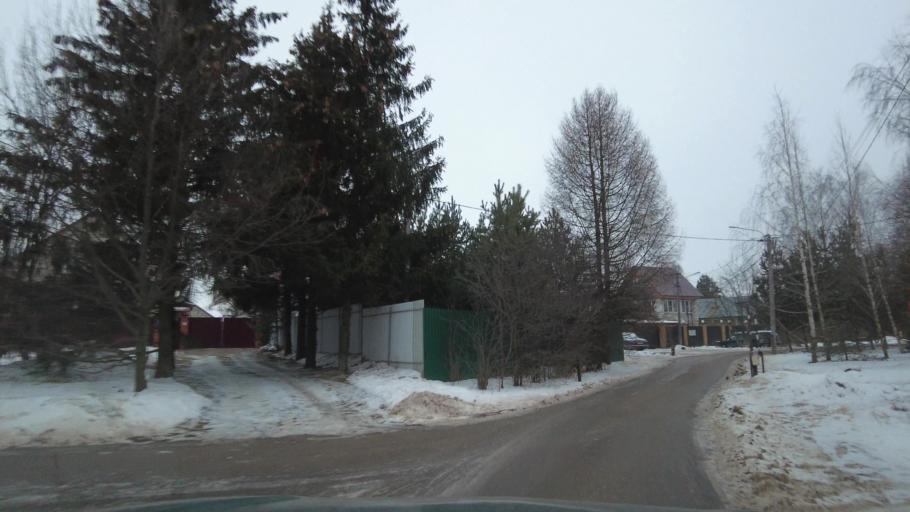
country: RU
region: Moskovskaya
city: Novopodrezkovo
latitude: 55.9795
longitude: 37.3849
